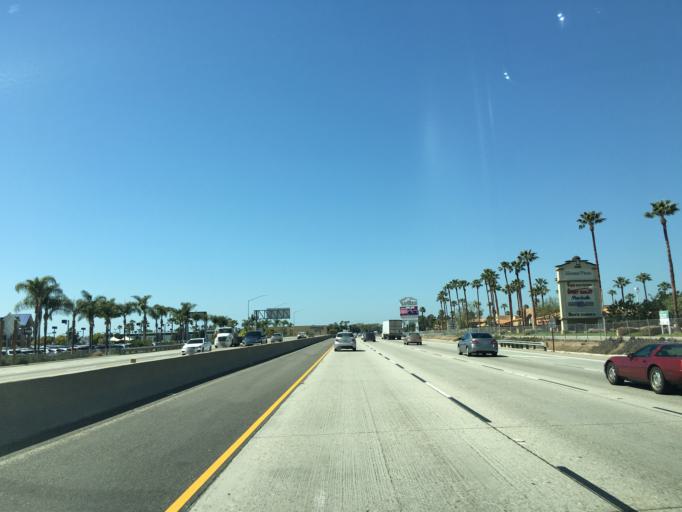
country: US
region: California
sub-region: Ventura County
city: El Rio
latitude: 34.2234
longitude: -119.1501
